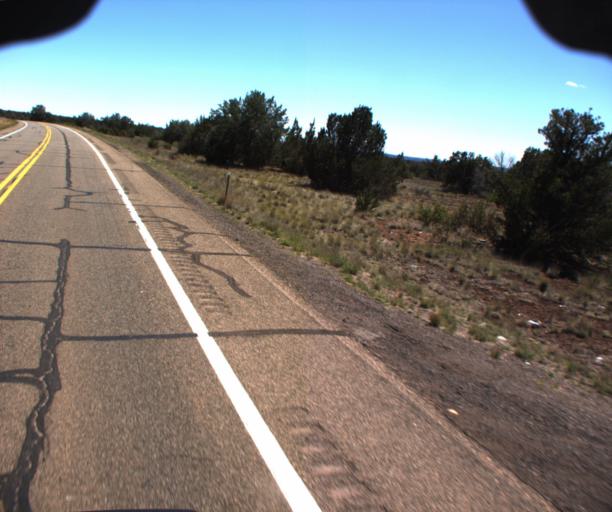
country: US
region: Arizona
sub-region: Coconino County
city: Williams
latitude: 35.2055
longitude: -112.4756
